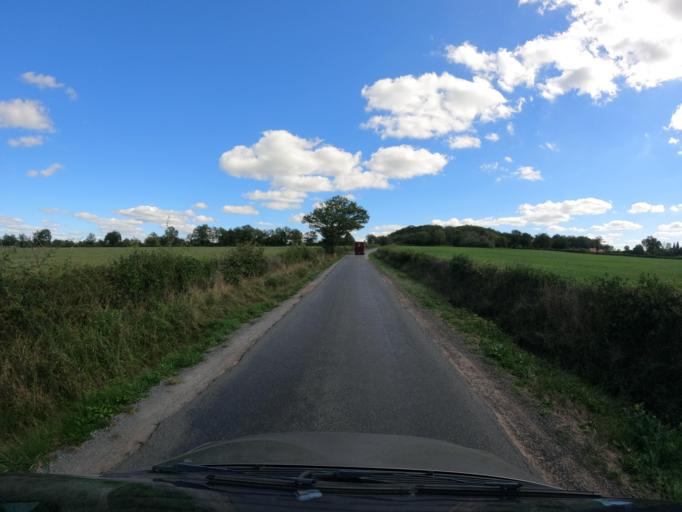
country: FR
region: Auvergne
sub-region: Departement de l'Allier
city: Doyet
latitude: 46.3864
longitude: 2.7705
